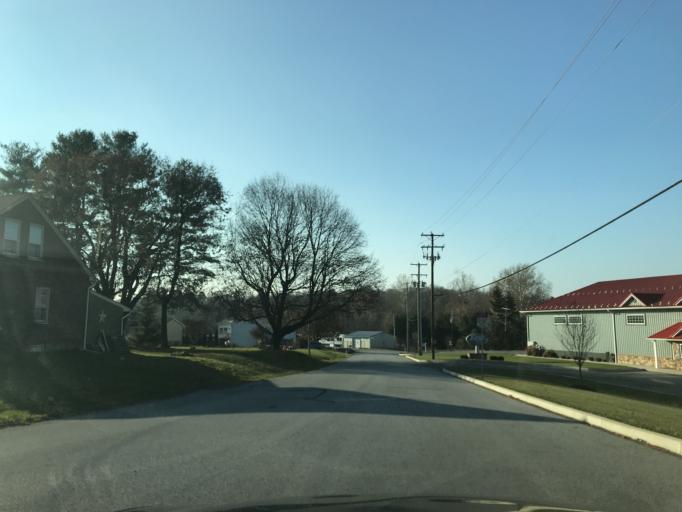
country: US
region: Pennsylvania
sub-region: York County
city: New Freedom
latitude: 39.7437
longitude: -76.6942
